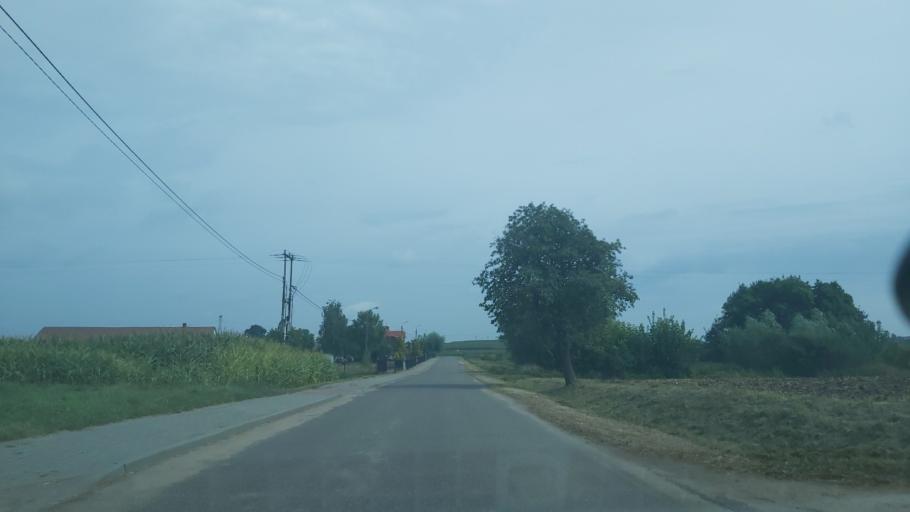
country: PL
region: Kujawsko-Pomorskie
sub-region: Powiat golubsko-dobrzynski
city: Zbojno
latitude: 53.0334
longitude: 19.1726
